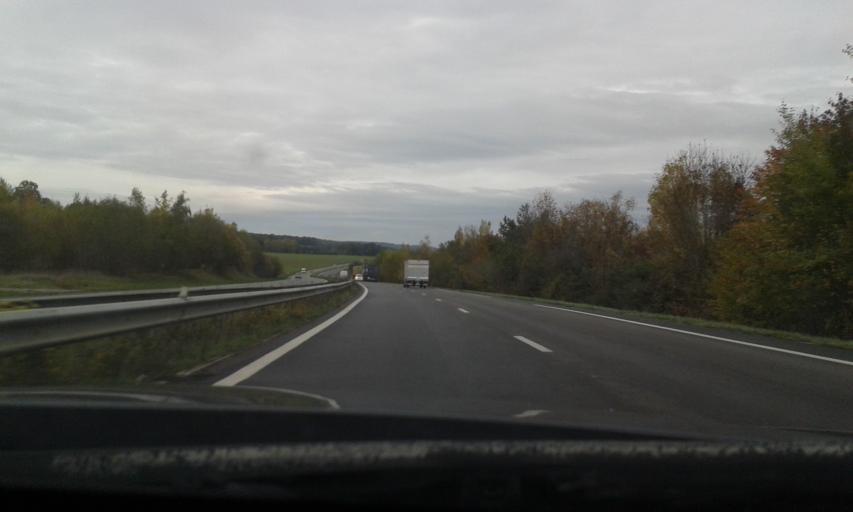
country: FR
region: Haute-Normandie
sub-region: Departement de l'Eure
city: Heudreville-sur-Eure
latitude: 49.1201
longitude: 1.1880
